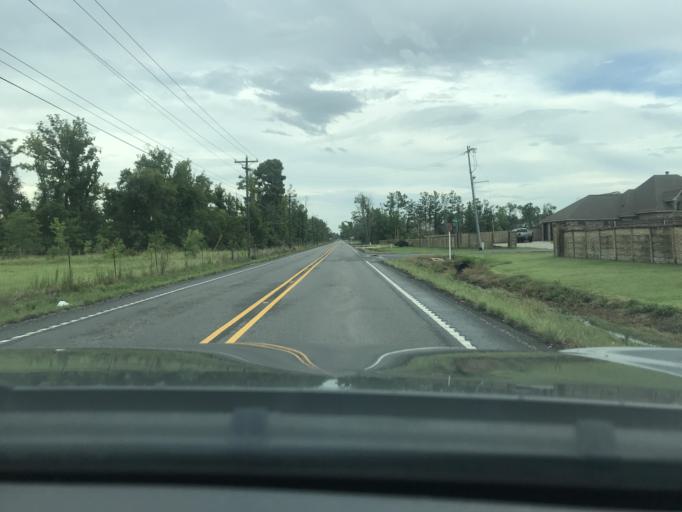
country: US
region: Louisiana
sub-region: Calcasieu Parish
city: Moss Bluff
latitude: 30.3107
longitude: -93.2583
